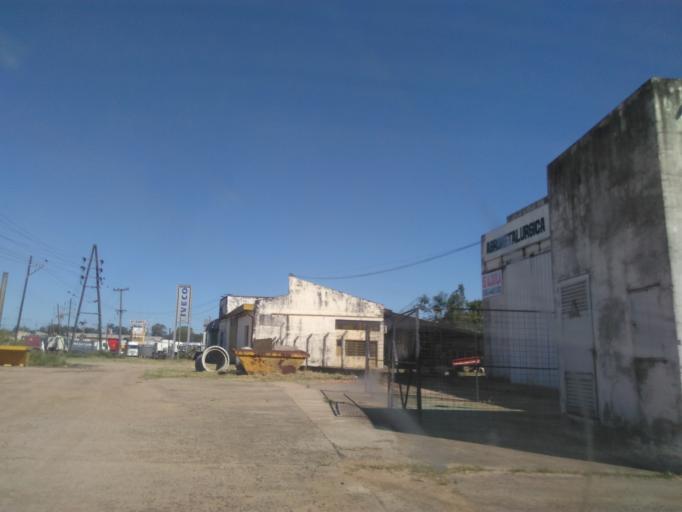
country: AR
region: Chaco
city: Fontana
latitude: -27.4217
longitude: -59.0088
